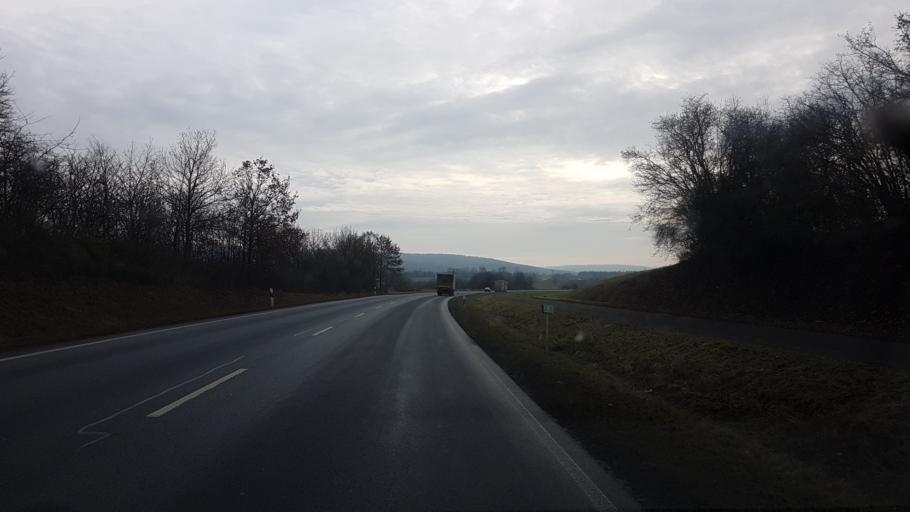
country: DE
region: Bavaria
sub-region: Regierungsbezirk Unterfranken
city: Pfarrweisach
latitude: 50.1379
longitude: 10.7532
